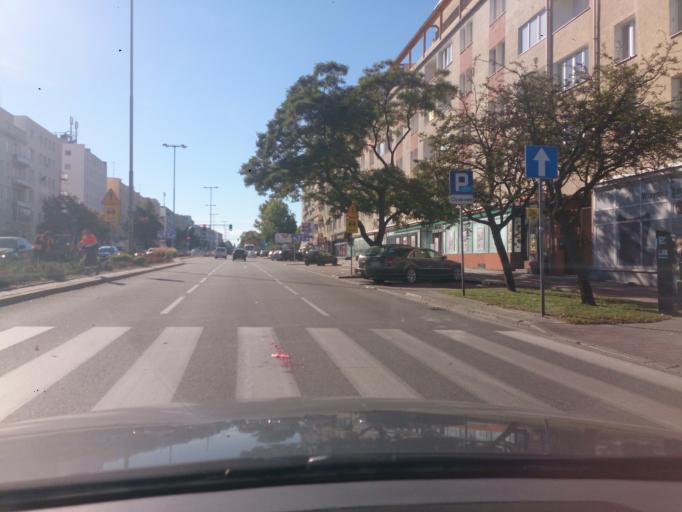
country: PL
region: Pomeranian Voivodeship
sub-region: Gdynia
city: Gdynia
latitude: 54.5162
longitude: 18.5385
